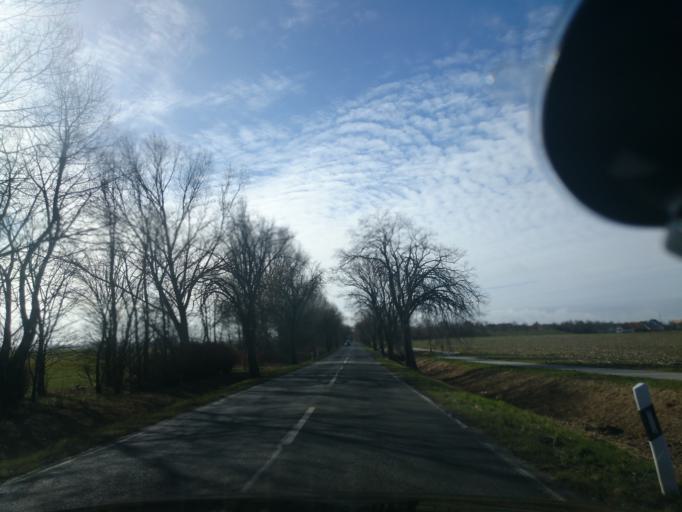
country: DE
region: Mecklenburg-Vorpommern
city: Elmenhorst
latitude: 54.1609
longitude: 12.0307
